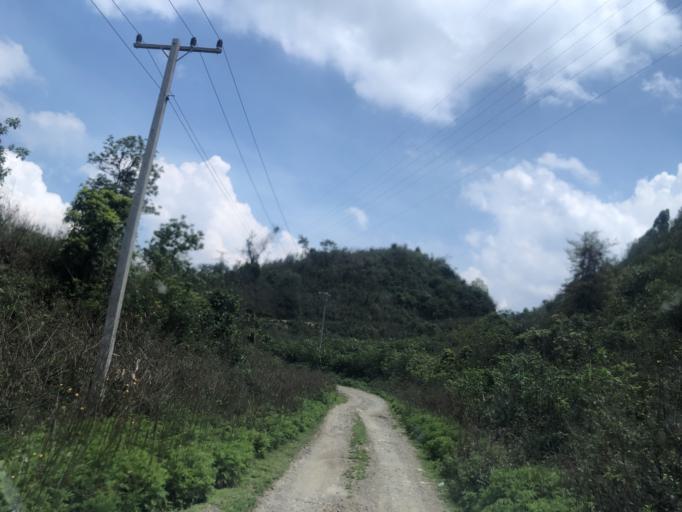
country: LA
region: Phongsali
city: Phongsali
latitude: 21.3913
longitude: 102.1922
